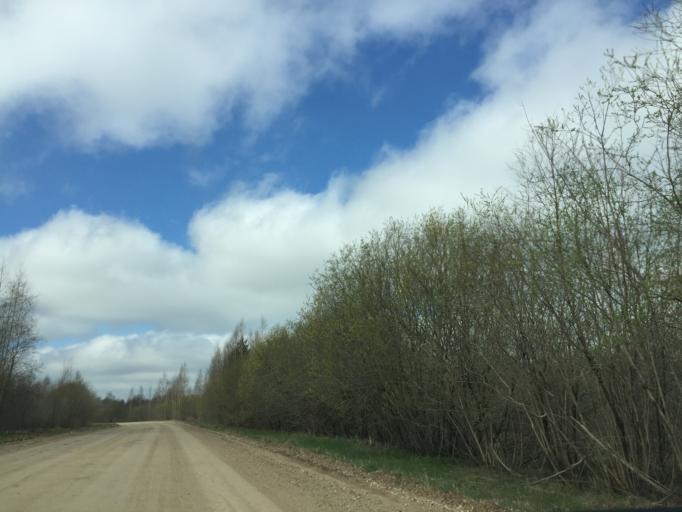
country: EE
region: Valgamaa
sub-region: Valga linn
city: Valga
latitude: 57.5412
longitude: 26.3236
